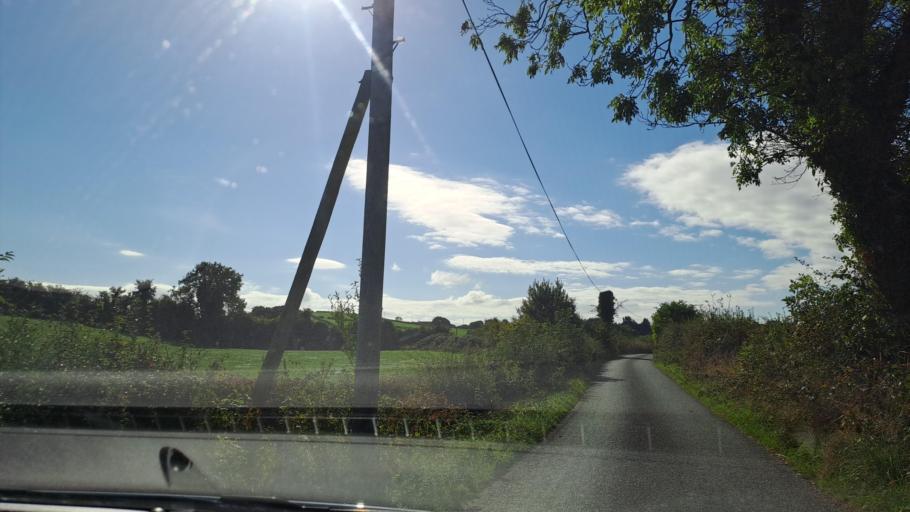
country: IE
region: Ulster
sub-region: County Monaghan
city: Carrickmacross
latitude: 53.9971
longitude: -6.7806
